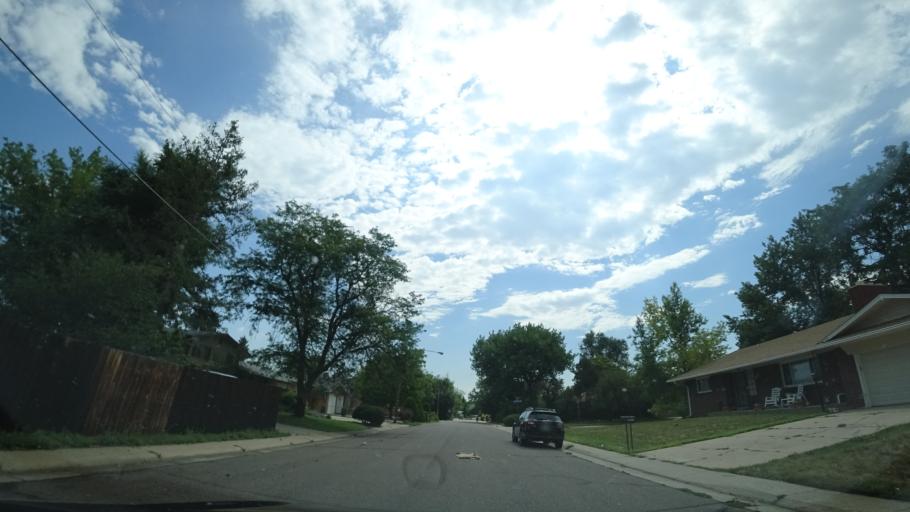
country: US
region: Colorado
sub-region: Jefferson County
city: Lakewood
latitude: 39.7239
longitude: -105.0667
